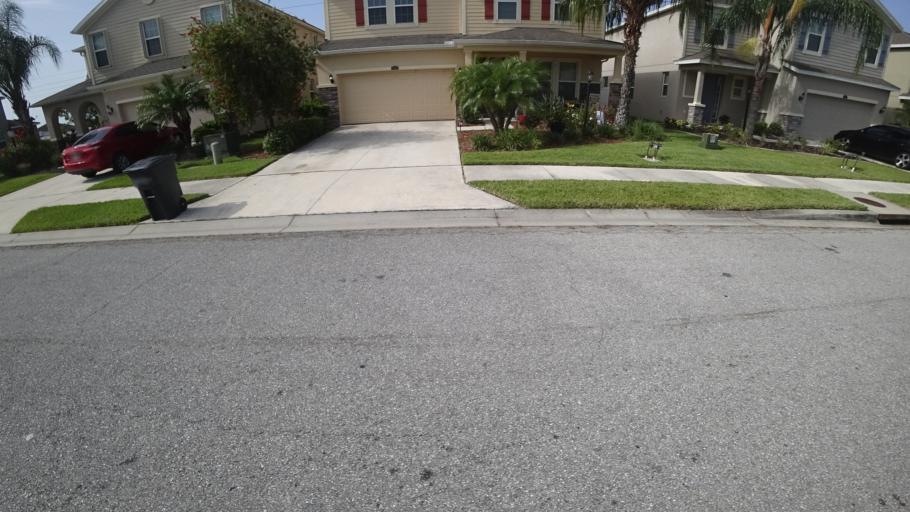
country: US
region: Florida
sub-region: Manatee County
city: Ellenton
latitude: 27.5527
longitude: -82.5064
